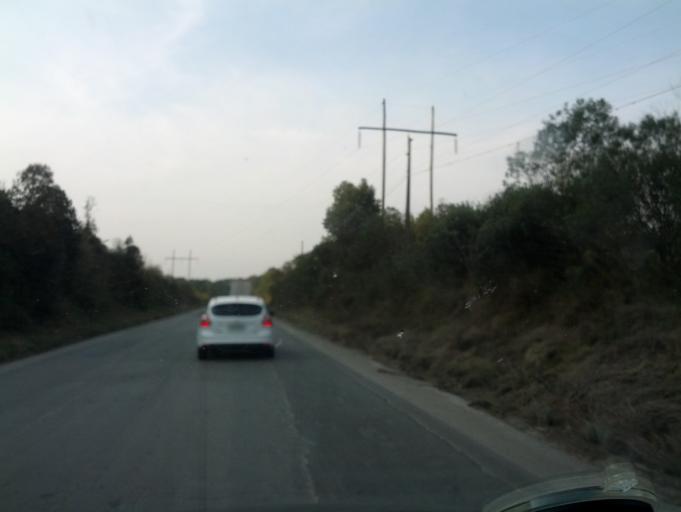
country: BR
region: Santa Catarina
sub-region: Otacilio Costa
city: Otacilio Costa
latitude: -27.5398
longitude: -50.1445
